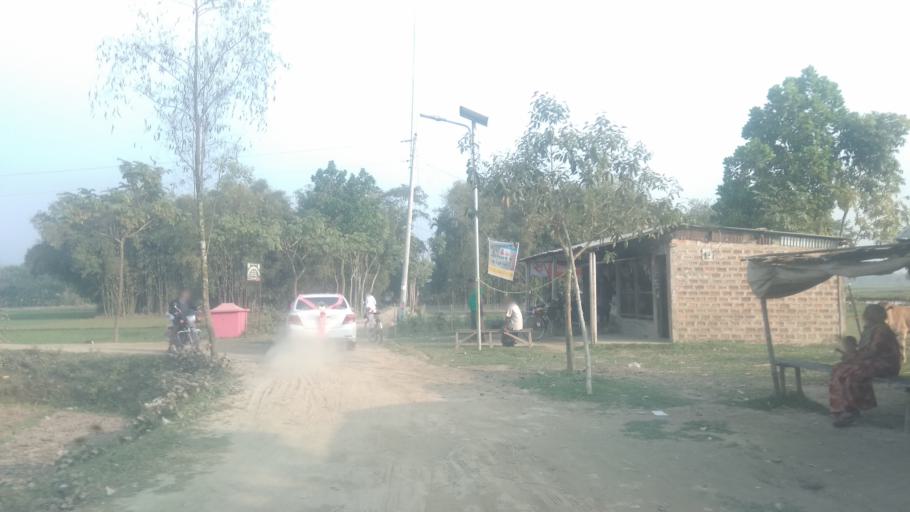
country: BD
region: Dhaka
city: Netrakona
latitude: 24.7742
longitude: 90.6097
